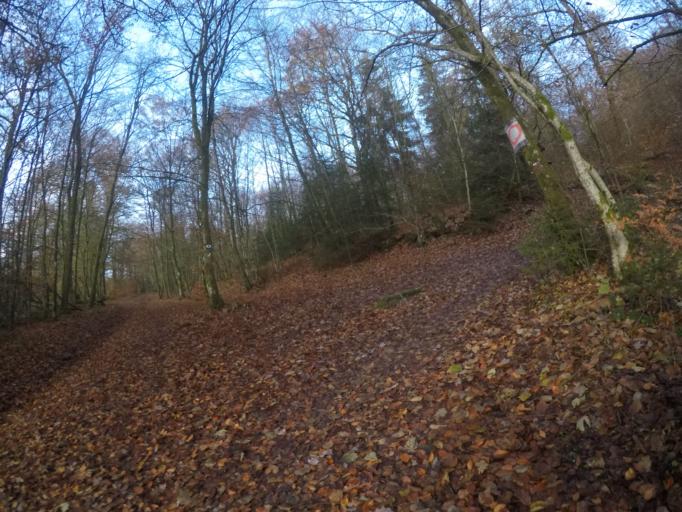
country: BE
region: Wallonia
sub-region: Province du Luxembourg
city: Habay-la-Vieille
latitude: 49.7404
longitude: 5.6703
